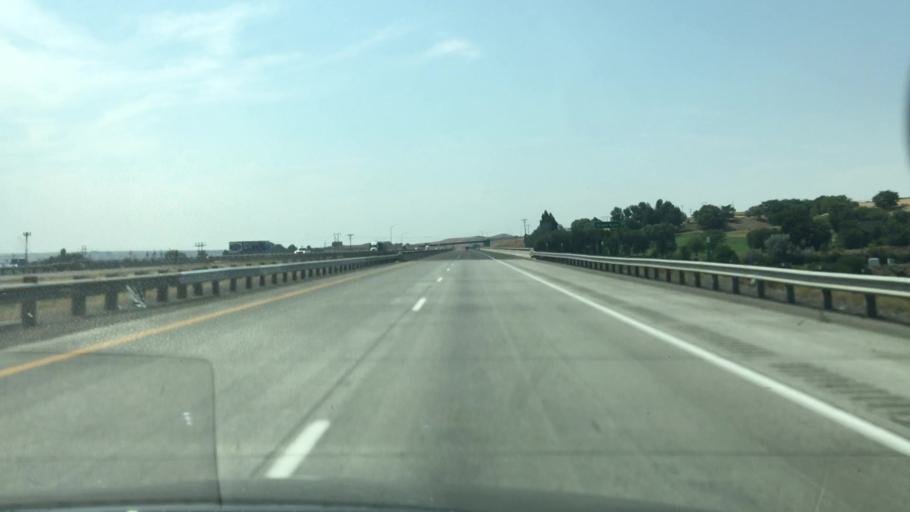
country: US
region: Idaho
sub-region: Elmore County
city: Glenns Ferry
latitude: 42.9609
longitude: -115.2767
